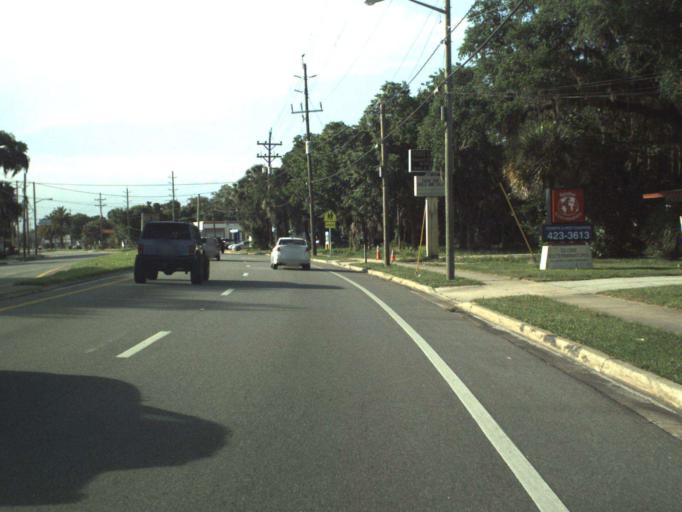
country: US
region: Florida
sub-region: Volusia County
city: New Smyrna Beach
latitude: 29.0292
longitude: -80.9282
